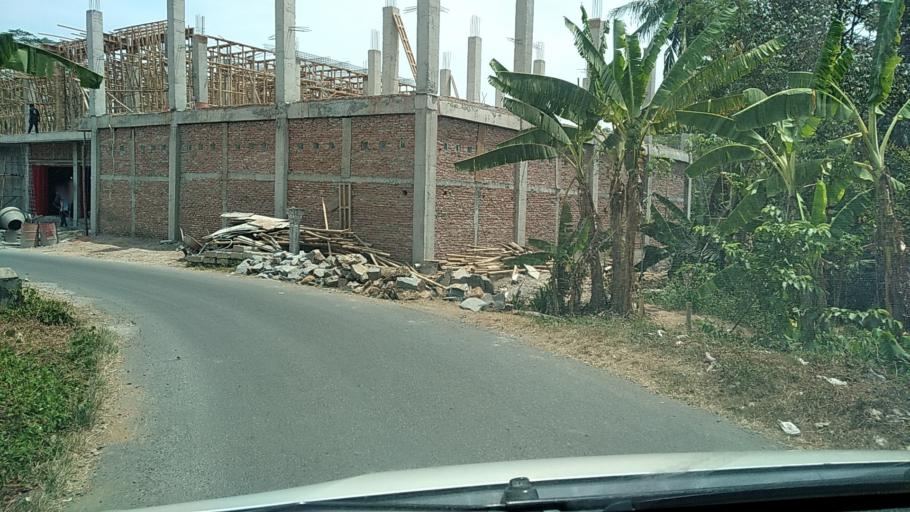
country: ID
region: Central Java
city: Ungaran
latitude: -7.0999
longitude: 110.3326
